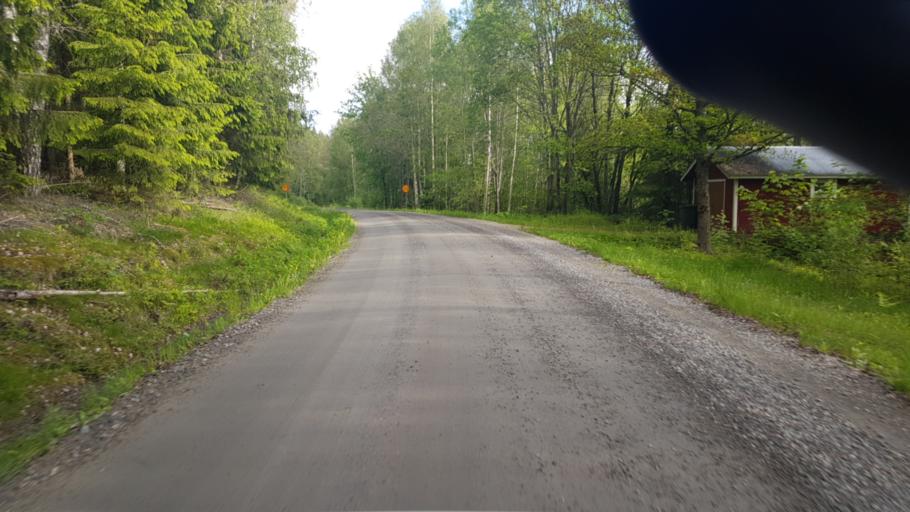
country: SE
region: Vaermland
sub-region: Eda Kommun
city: Amotfors
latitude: 59.7360
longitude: 12.2789
